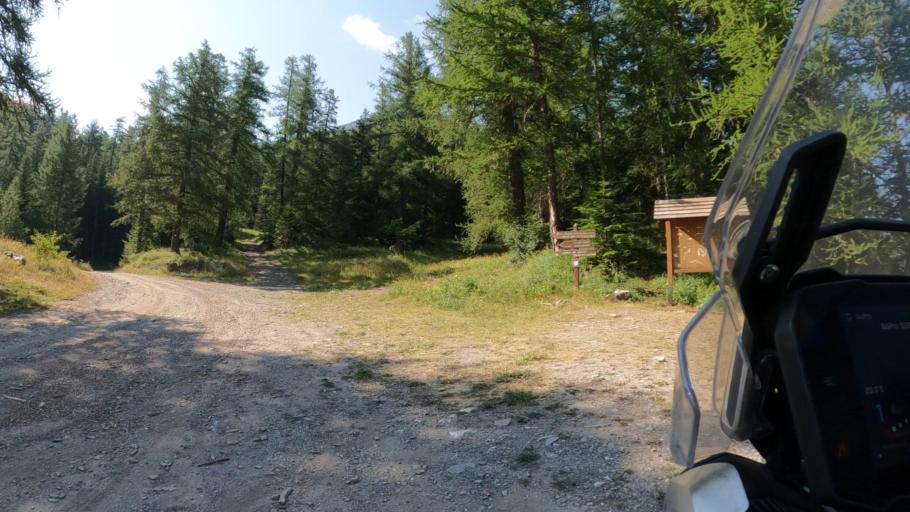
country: FR
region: Provence-Alpes-Cote d'Azur
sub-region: Departement des Hautes-Alpes
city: Embrun
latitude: 44.5935
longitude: 6.5693
